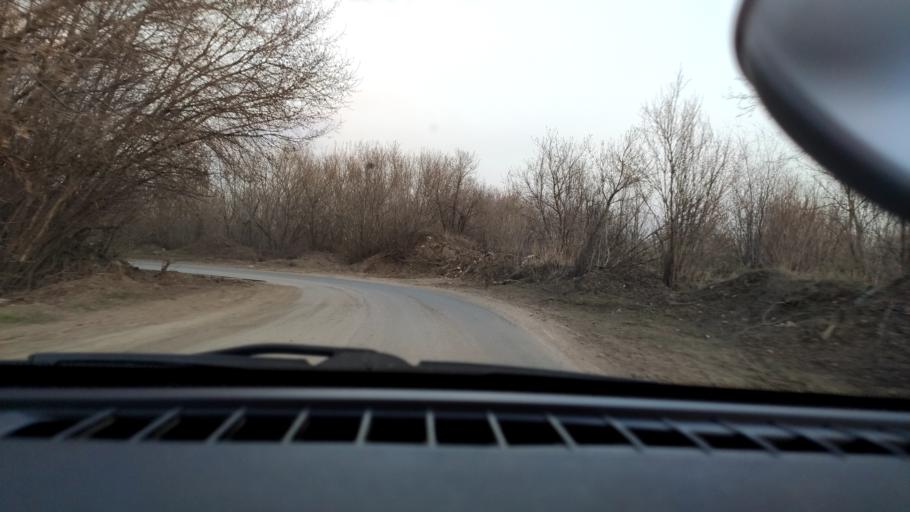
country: RU
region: Samara
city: Smyshlyayevka
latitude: 53.2060
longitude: 50.3143
